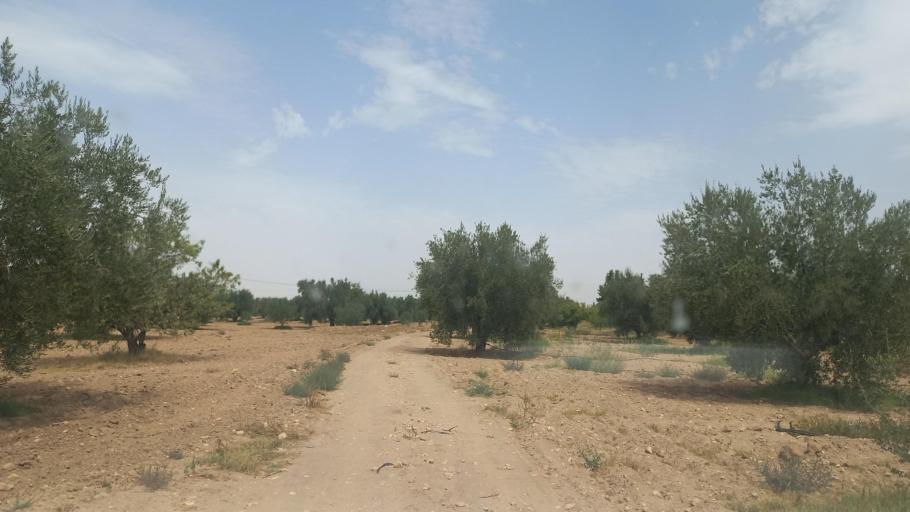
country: TN
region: Al Qasrayn
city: Kasserine
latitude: 35.2586
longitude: 8.9996
